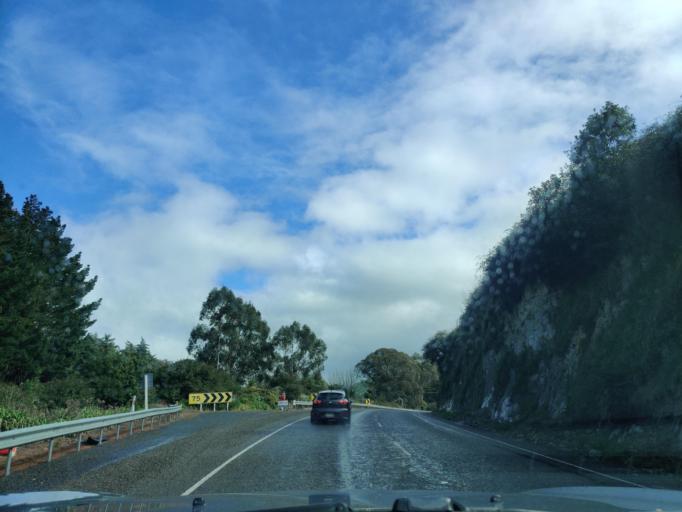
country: NZ
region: Hawke's Bay
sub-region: Hastings District
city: Hastings
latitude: -39.7183
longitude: 176.7758
